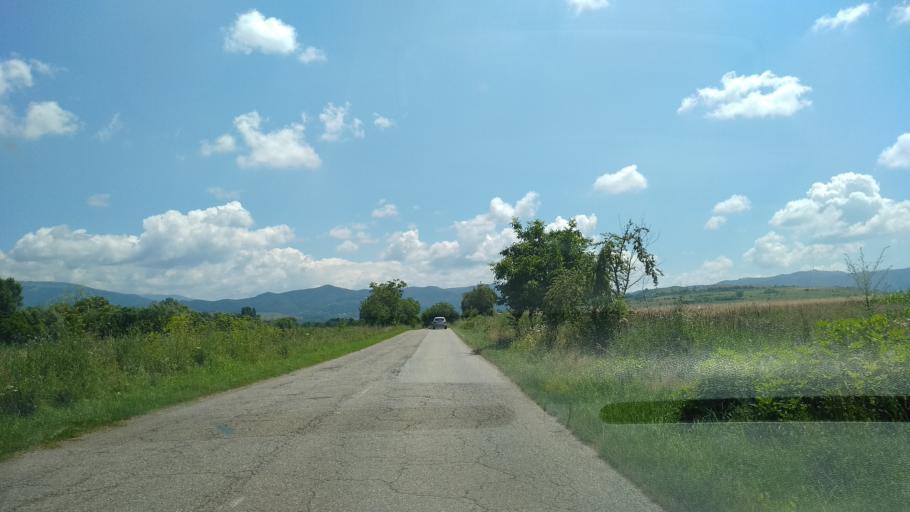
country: RO
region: Hunedoara
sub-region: Comuna Bosorod
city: Bosorod
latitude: 45.7112
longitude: 23.0454
